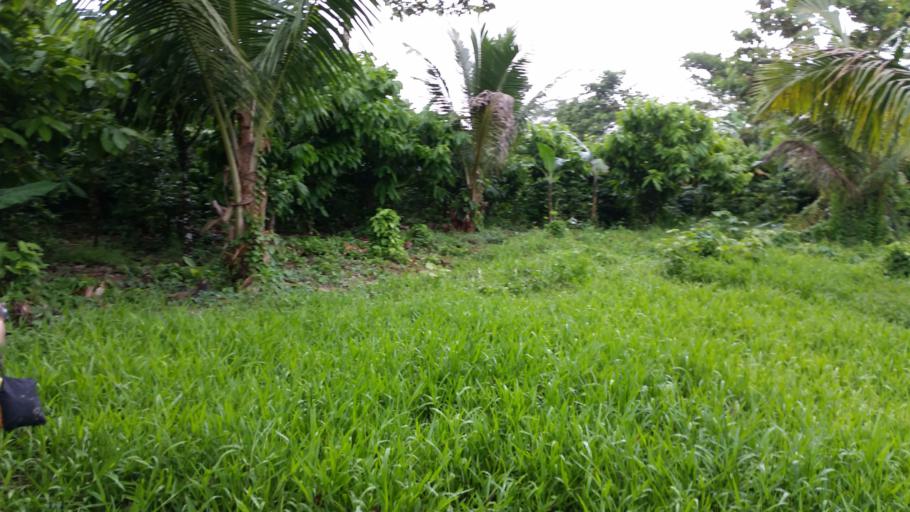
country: NI
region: Atlantico Norte (RAAN)
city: Bonanza
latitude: 14.0961
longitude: -84.6769
